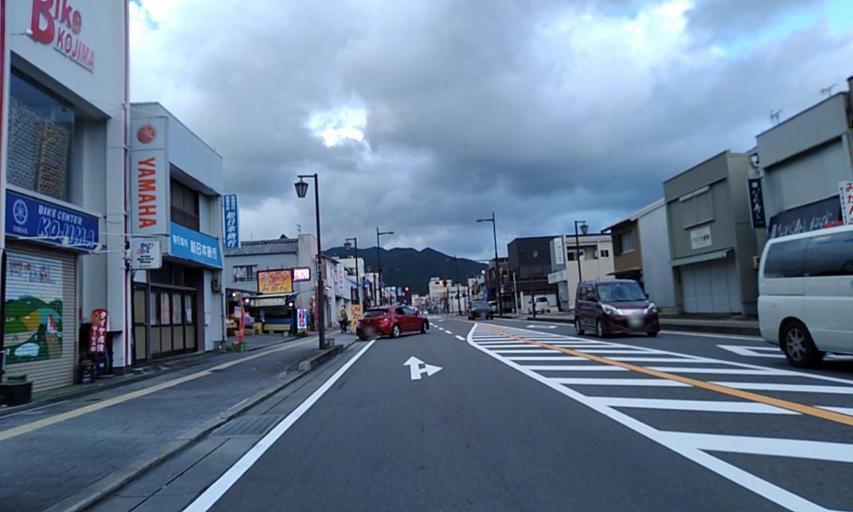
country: JP
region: Wakayama
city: Shingu
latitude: 33.7232
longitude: 135.9865
